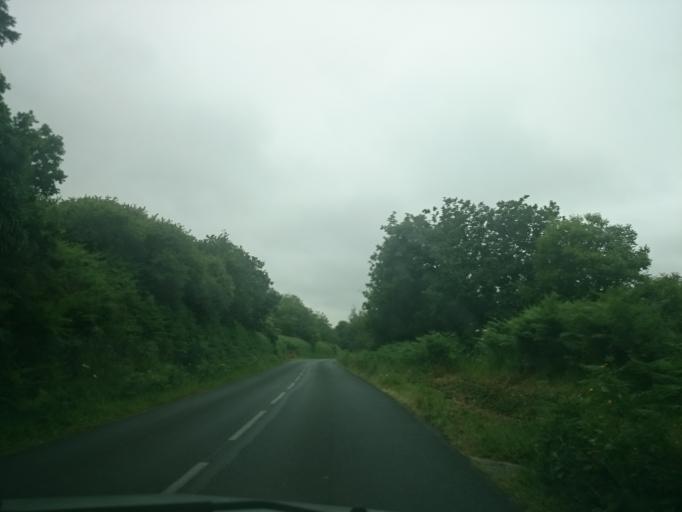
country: FR
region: Brittany
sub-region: Departement du Finistere
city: Saint-Pabu
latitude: 48.5557
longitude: -4.5869
